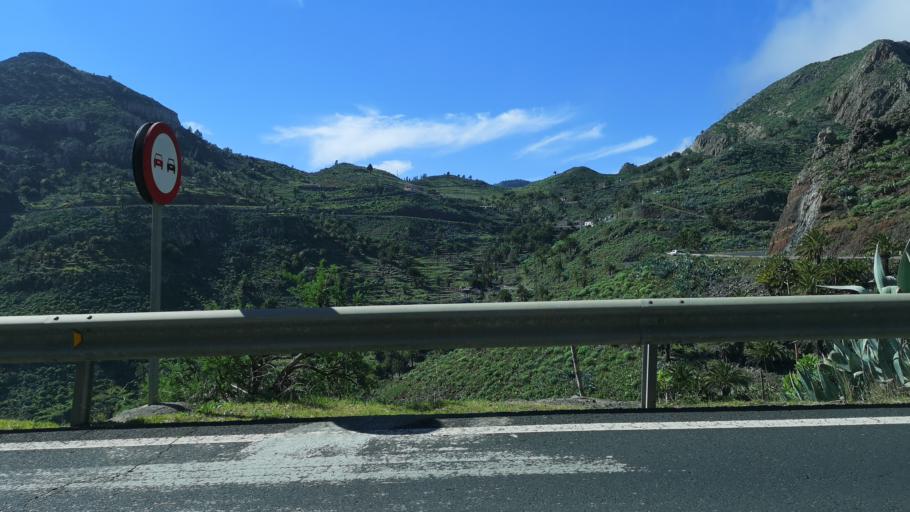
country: ES
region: Canary Islands
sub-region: Provincia de Santa Cruz de Tenerife
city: Alajero
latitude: 28.0939
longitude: -17.1971
